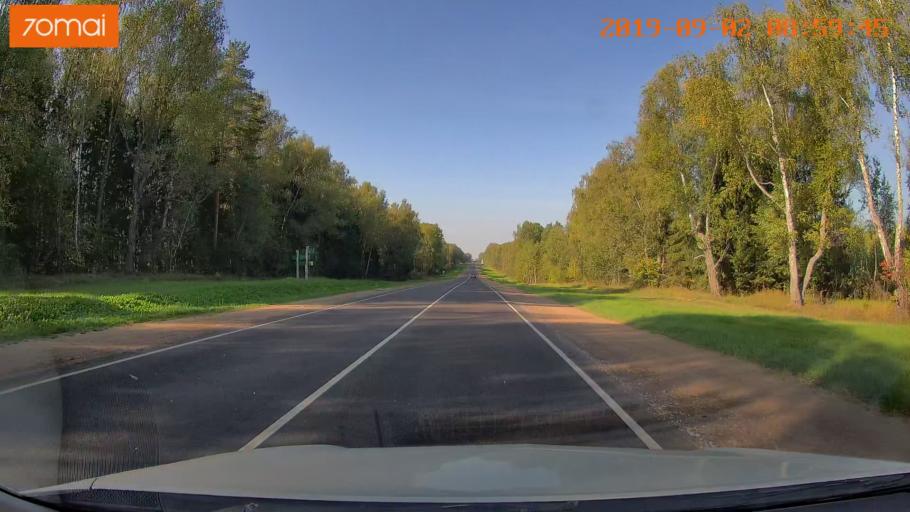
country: RU
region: Kaluga
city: Myatlevo
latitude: 54.9184
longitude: 35.7233
